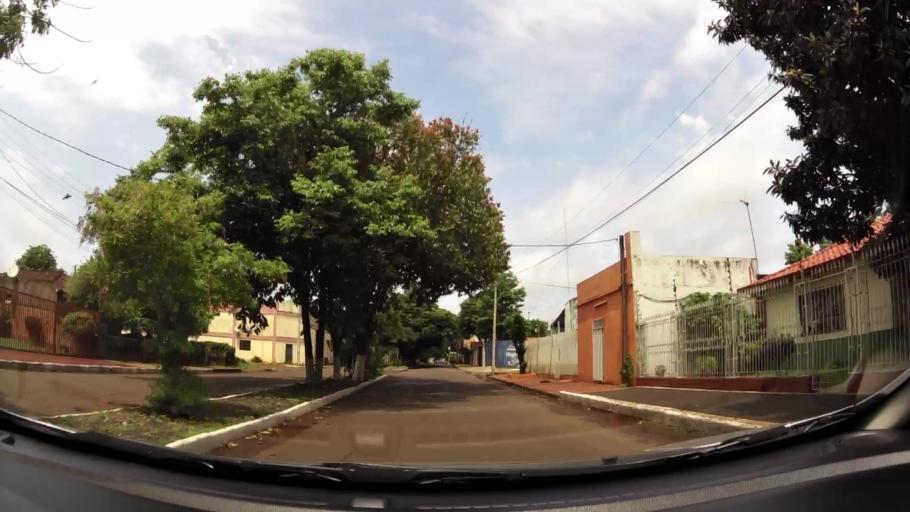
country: PY
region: Alto Parana
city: Ciudad del Este
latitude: -25.5059
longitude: -54.6631
